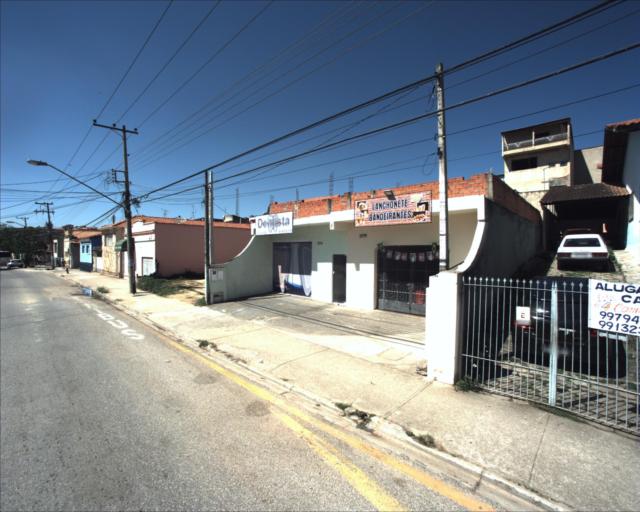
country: BR
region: Sao Paulo
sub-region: Votorantim
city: Votorantim
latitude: -23.5075
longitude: -47.3683
